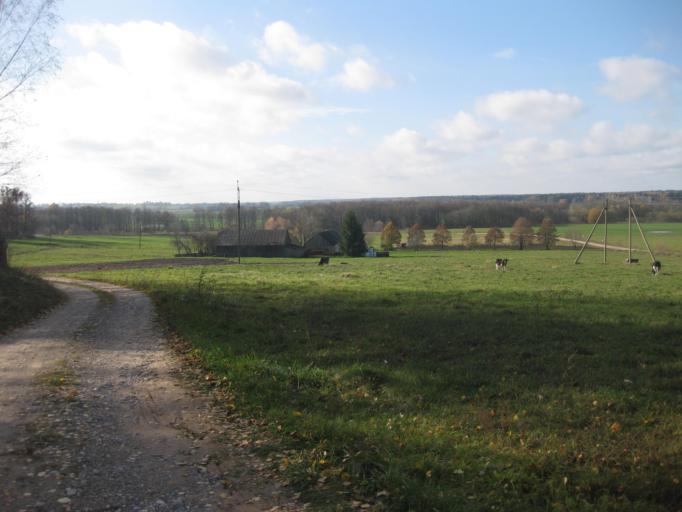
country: LT
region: Kauno apskritis
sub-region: Kauno rajonas
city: Mastaiciai
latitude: 54.6687
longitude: 23.7571
